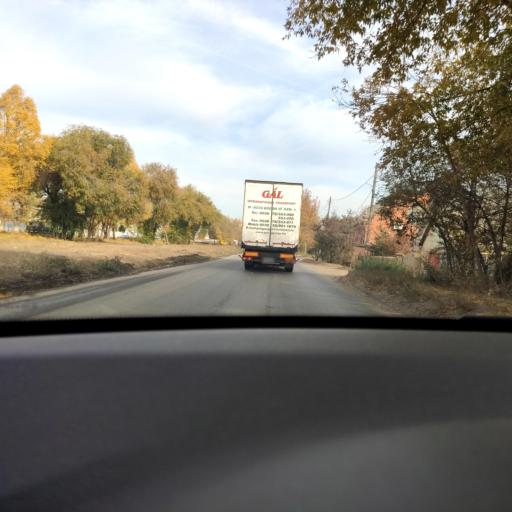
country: RU
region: Samara
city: Petra-Dubrava
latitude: 53.2412
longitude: 50.3087
